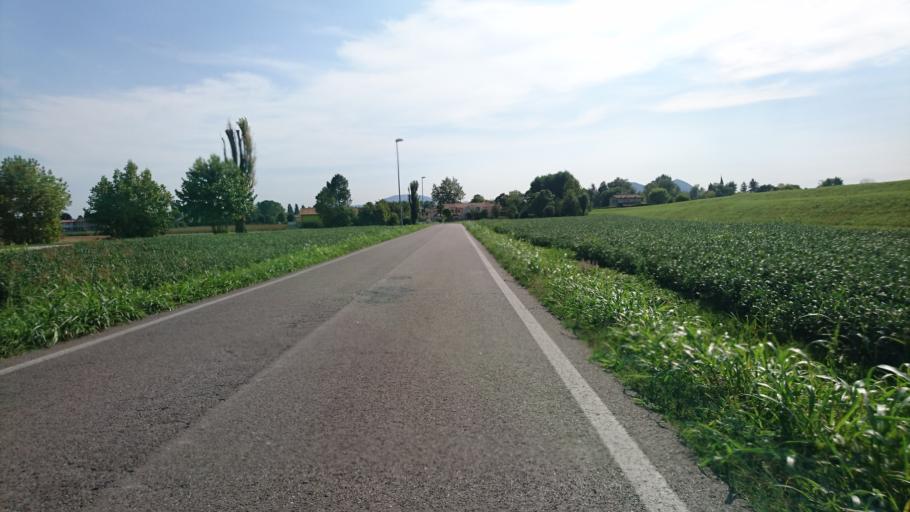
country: IT
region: Veneto
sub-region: Provincia di Padova
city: Saccolongo
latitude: 45.4175
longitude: 11.7484
